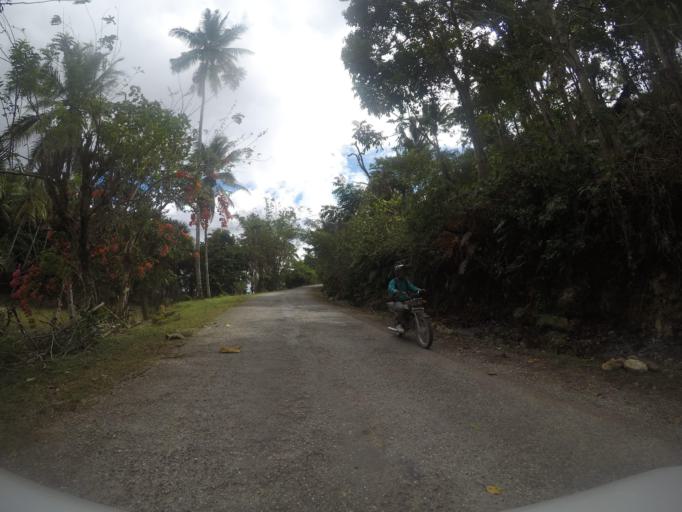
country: TL
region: Lautem
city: Lospalos
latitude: -8.5381
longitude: 126.9391
